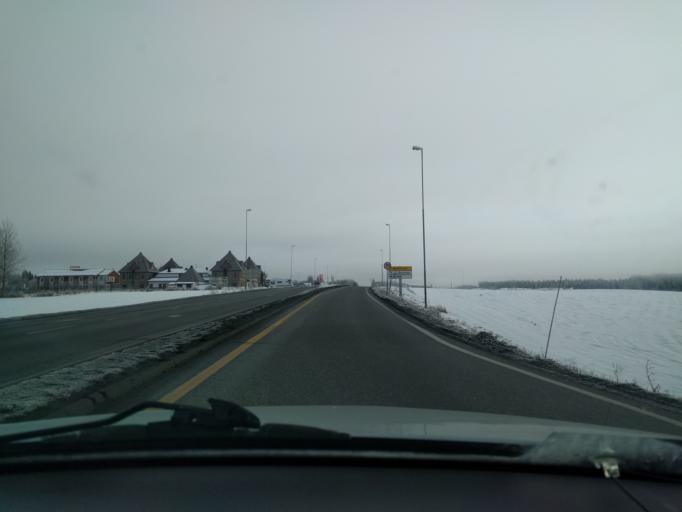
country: NO
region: Hedmark
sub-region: Loten
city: Loten
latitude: 60.8478
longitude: 11.3650
